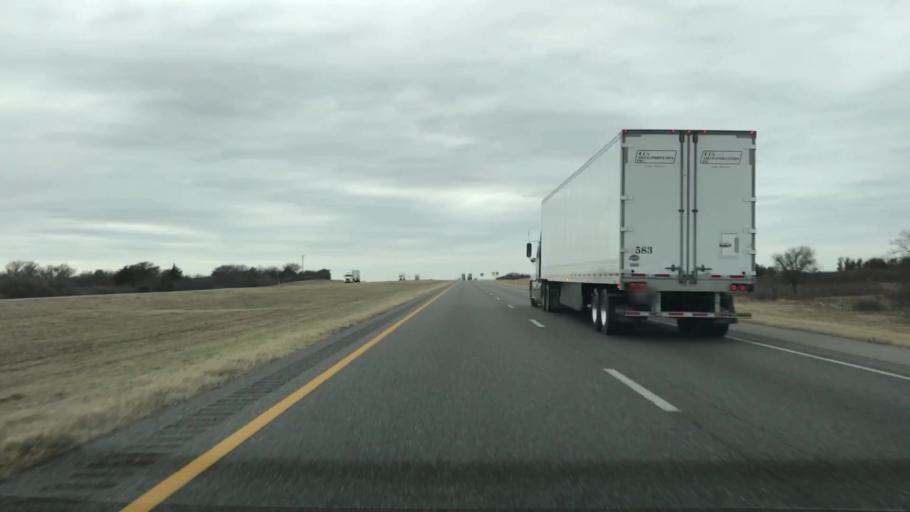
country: US
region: Oklahoma
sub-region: Beckham County
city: Erick
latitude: 35.2265
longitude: -99.9034
